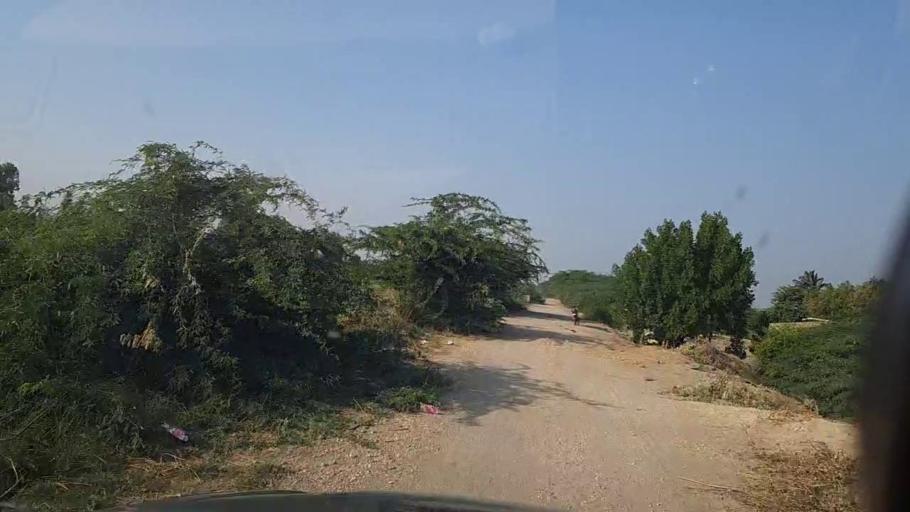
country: PK
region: Sindh
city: Thatta
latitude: 24.6169
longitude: 67.8762
